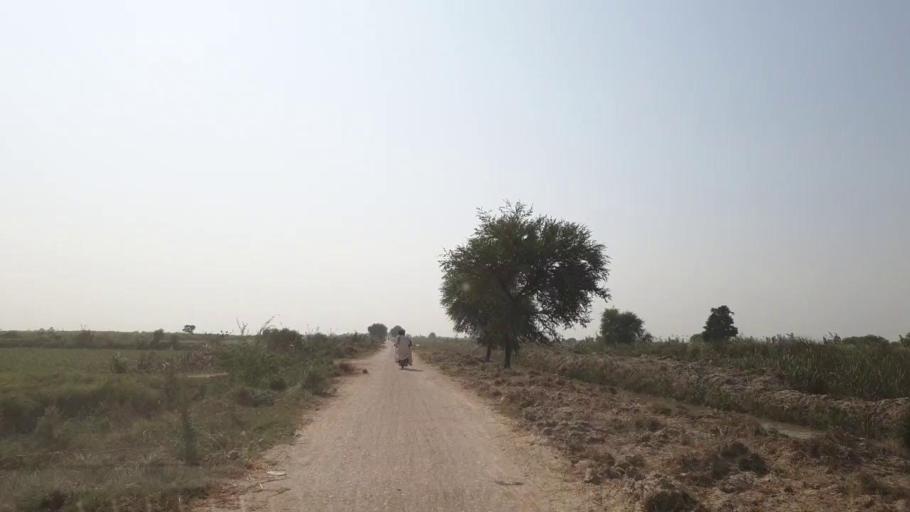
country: PK
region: Sindh
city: Bulri
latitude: 24.9741
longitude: 68.3998
